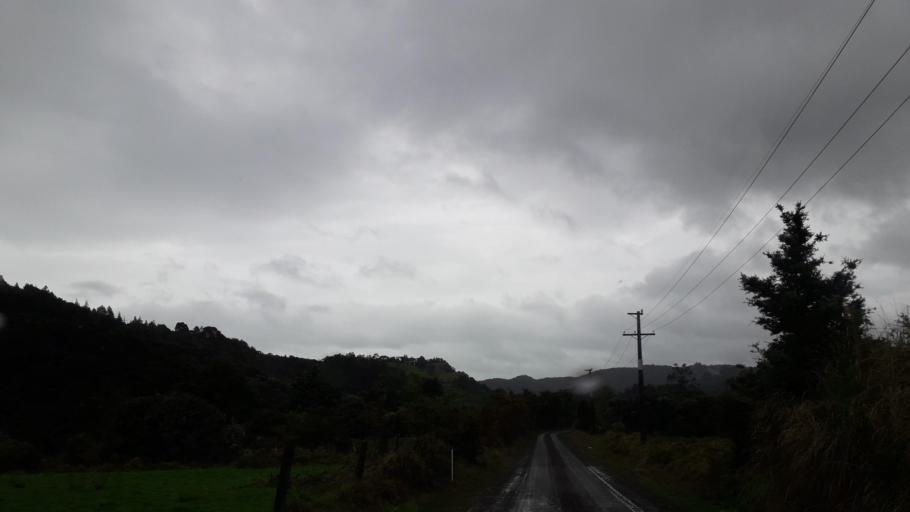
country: NZ
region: Northland
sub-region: Far North District
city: Kaitaia
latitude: -35.3775
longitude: 173.4112
